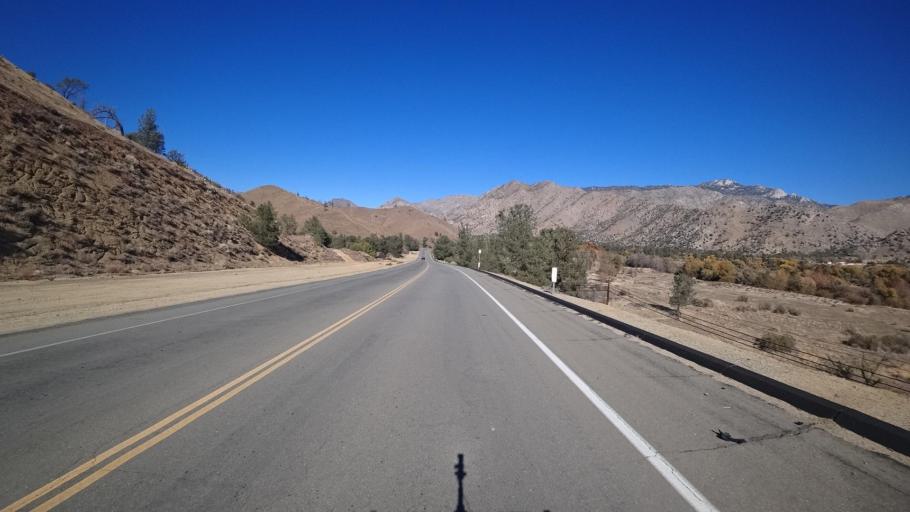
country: US
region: California
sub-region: Kern County
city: Kernville
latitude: 35.7338
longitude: -118.4276
